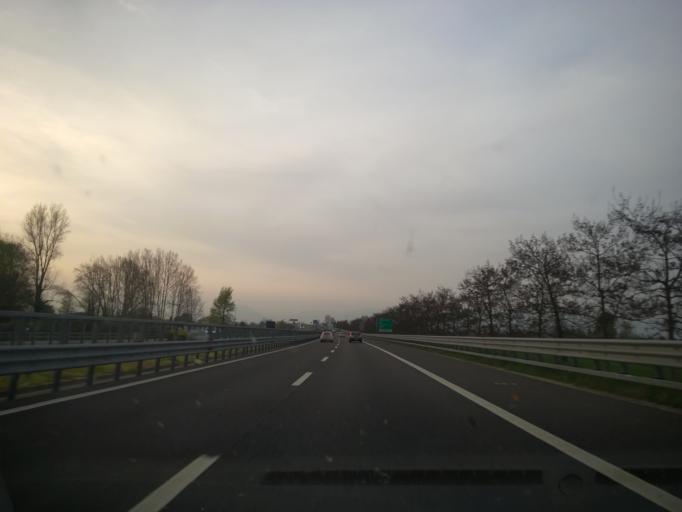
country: IT
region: Veneto
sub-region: Provincia di Vicenza
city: Lisiera
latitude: 45.5692
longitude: 11.6110
